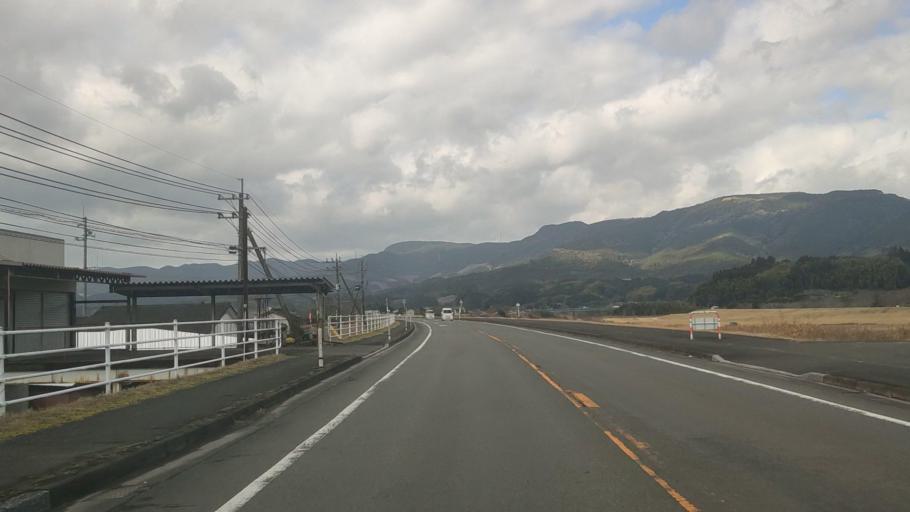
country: JP
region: Kumamoto
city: Hitoyoshi
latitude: 32.0547
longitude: 130.7980
